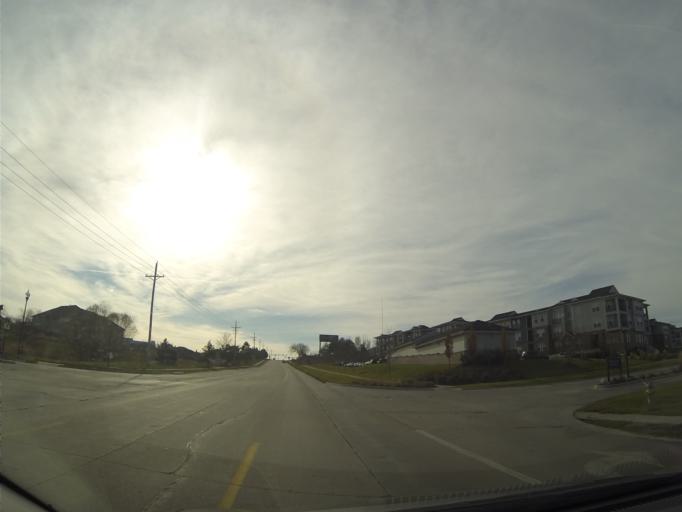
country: US
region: Nebraska
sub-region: Douglas County
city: Elkhorn
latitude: 41.2702
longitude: -96.2157
